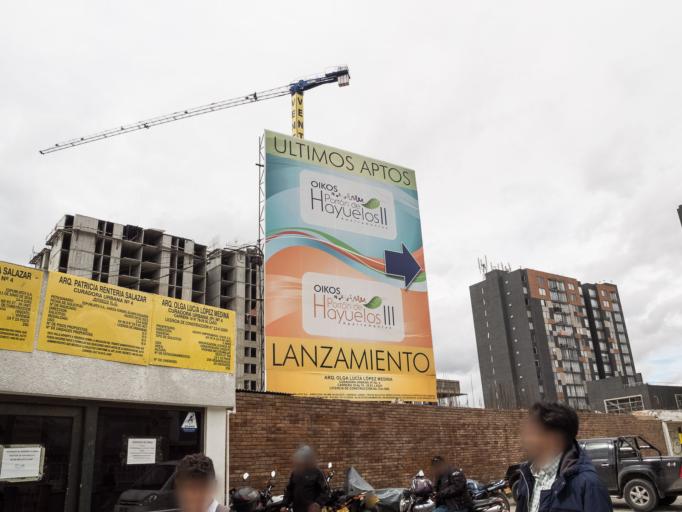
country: CO
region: Bogota D.C.
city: Bogota
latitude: 4.6694
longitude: -74.1384
